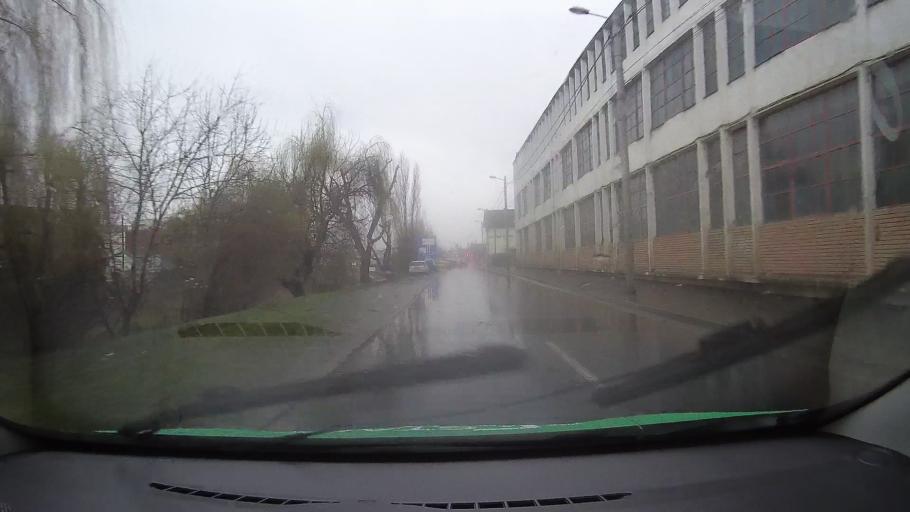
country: RO
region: Sibiu
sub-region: Municipiul Sibiu
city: Sibiu
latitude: 45.8020
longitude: 24.1453
